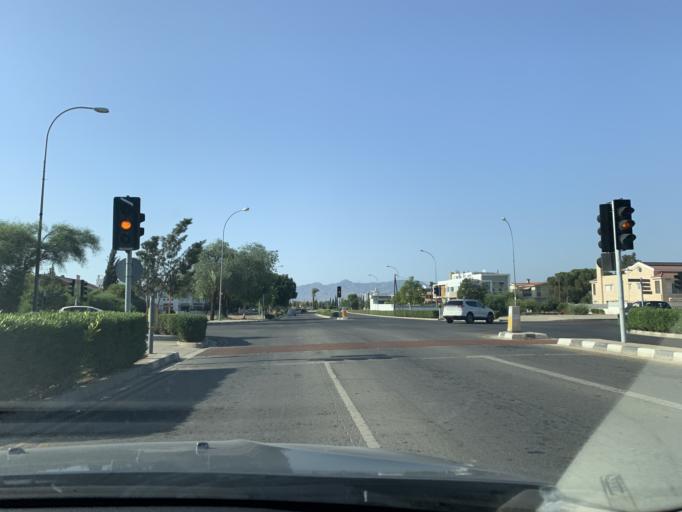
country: CY
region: Lefkosia
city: Nicosia
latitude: 35.1483
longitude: 33.3812
